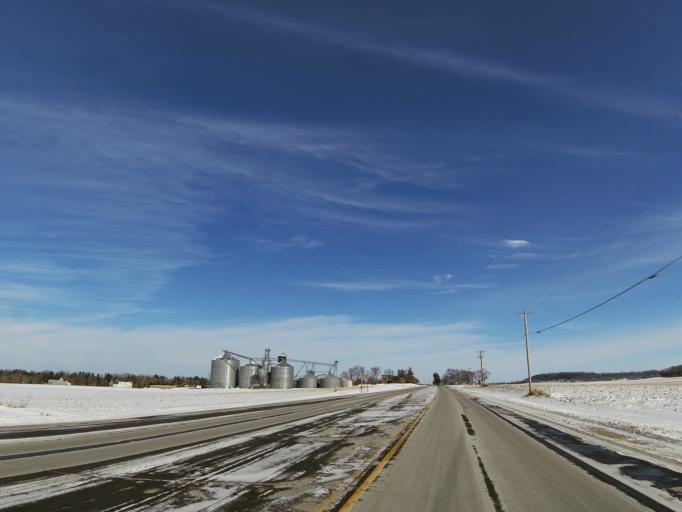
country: US
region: Wisconsin
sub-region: Pierce County
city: Prescott
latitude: 44.7646
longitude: -92.7882
